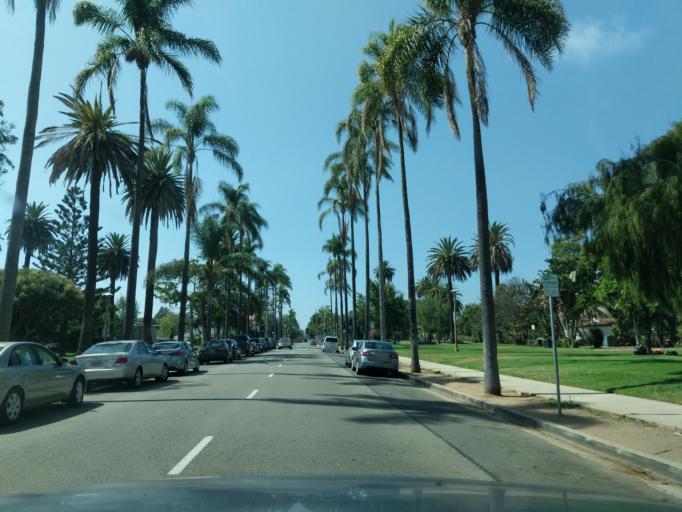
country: US
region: California
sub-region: Santa Barbara County
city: Santa Barbara
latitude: 34.4276
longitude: -119.7049
